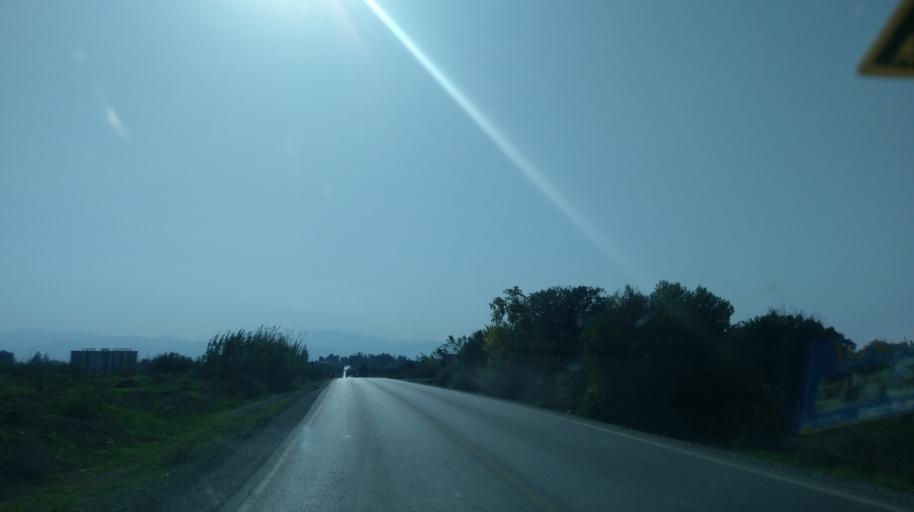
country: CY
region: Lefkosia
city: Morfou
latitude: 35.2157
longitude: 33.0045
